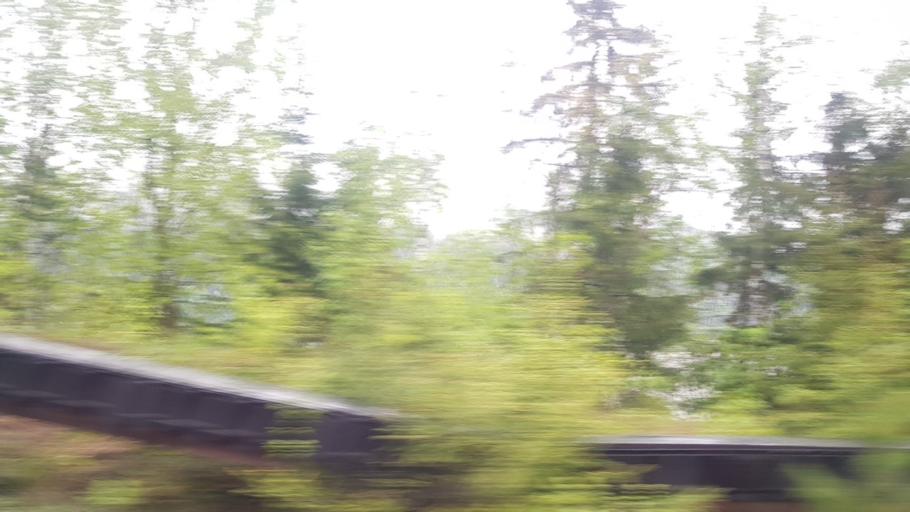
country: NO
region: Oppland
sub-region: Oyer
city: Tretten
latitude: 61.3908
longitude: 10.2412
